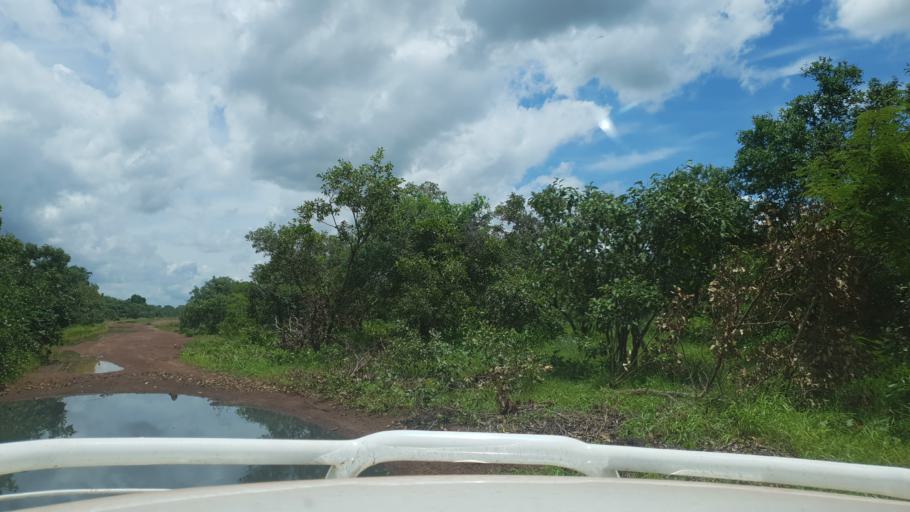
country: ML
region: Koulikoro
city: Banamba
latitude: 13.1988
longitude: -7.3291
